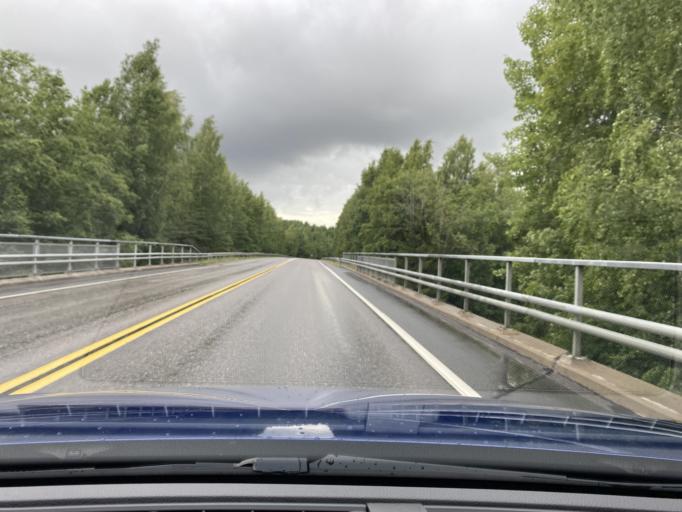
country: FI
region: Uusimaa
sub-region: Helsinki
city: Hyvinge
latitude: 60.5722
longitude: 24.8021
